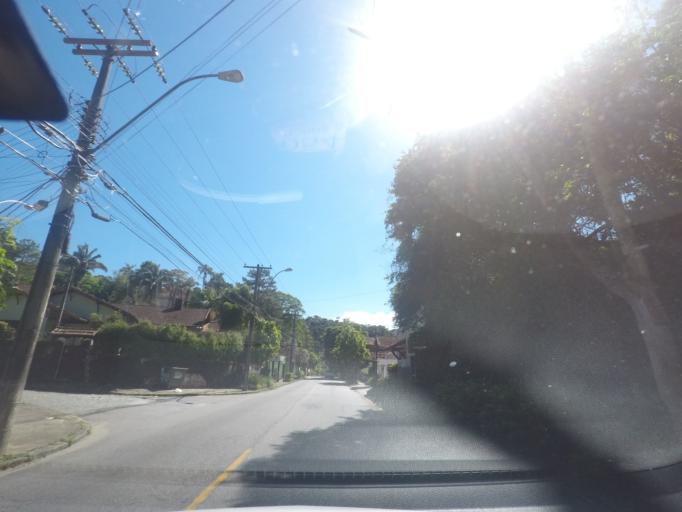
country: BR
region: Rio de Janeiro
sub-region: Petropolis
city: Petropolis
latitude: -22.5156
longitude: -43.1883
